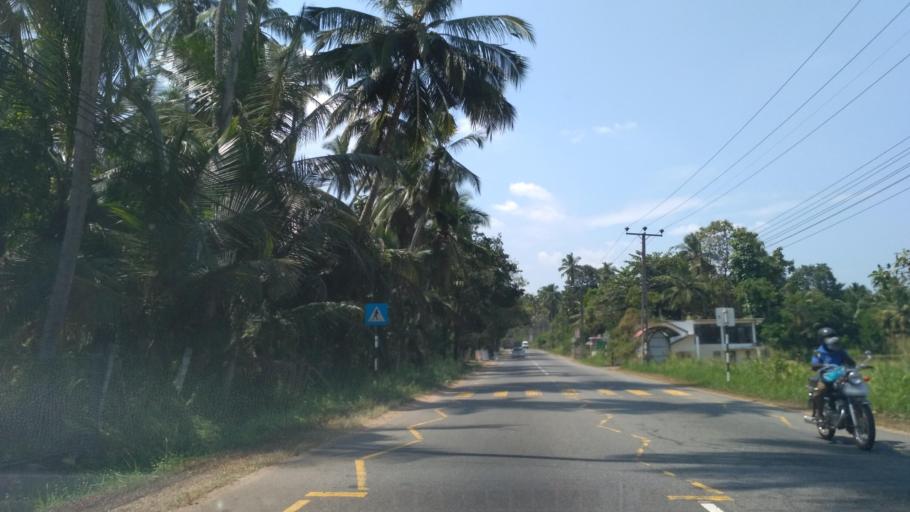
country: LK
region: North Western
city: Kurunegala
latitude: 7.4529
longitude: 80.2778
